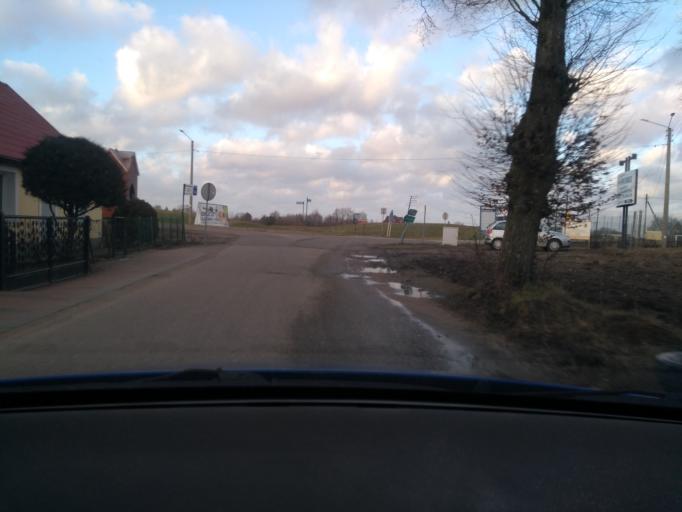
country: PL
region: Pomeranian Voivodeship
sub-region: Powiat kartuski
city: Przodkowo
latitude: 54.4002
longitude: 18.2235
